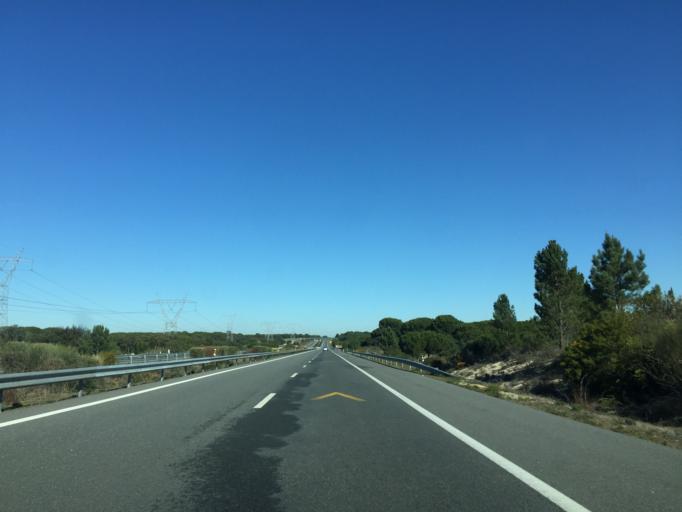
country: PT
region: Setubal
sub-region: Alcacer do Sal
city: Alcacer do Sal
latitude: 38.3113
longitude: -8.5080
